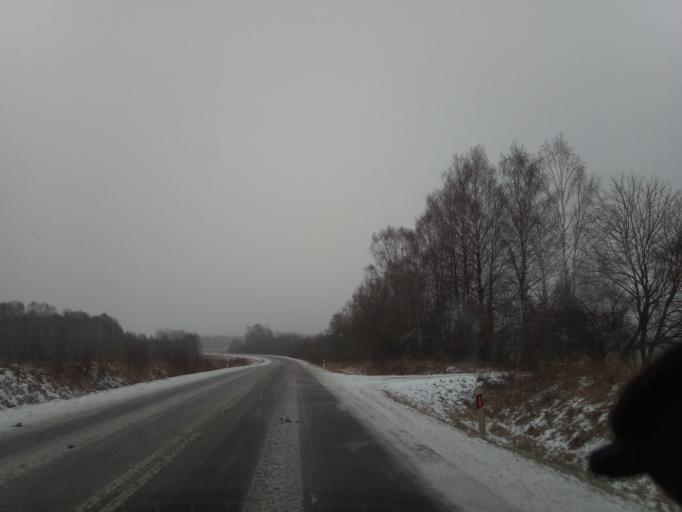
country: LT
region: Utenos apskritis
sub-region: Anyksciai
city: Anyksciai
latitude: 55.4022
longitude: 25.1371
